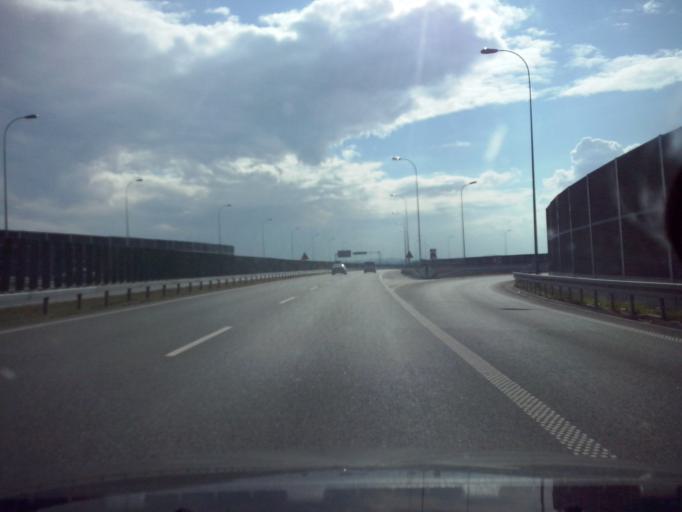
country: PL
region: Lesser Poland Voivodeship
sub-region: Powiat tarnowski
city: Wierzchoslawice
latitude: 50.0144
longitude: 20.8683
